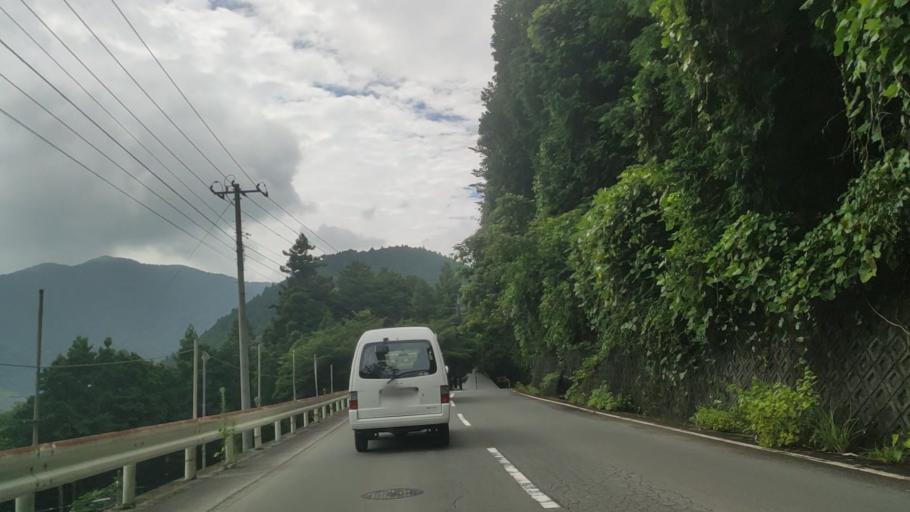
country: JP
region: Shizuoka
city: Fujinomiya
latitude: 35.2300
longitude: 138.5225
